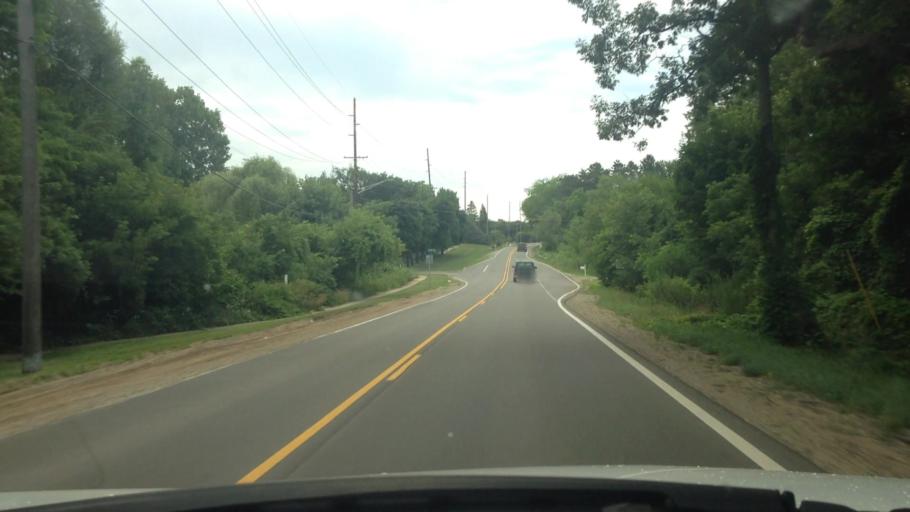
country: US
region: Michigan
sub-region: Oakland County
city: Waterford
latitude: 42.6997
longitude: -83.3487
